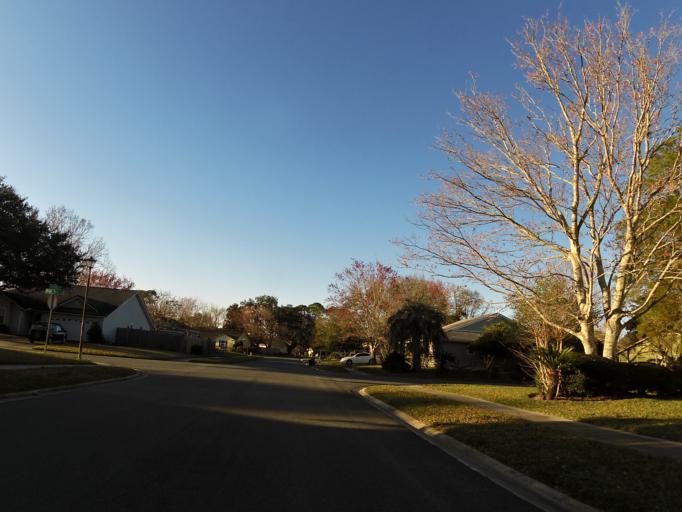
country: US
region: Florida
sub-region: Saint Johns County
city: Fruit Cove
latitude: 30.1735
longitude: -81.5799
